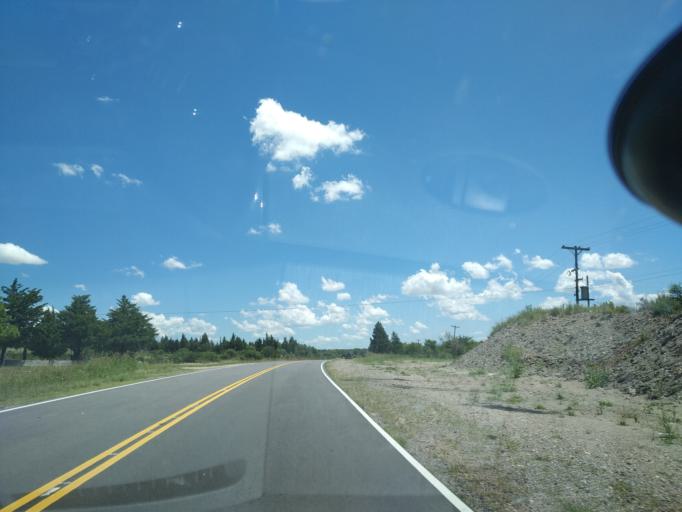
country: AR
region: Cordoba
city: Salsacate
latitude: -31.3521
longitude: -65.0963
